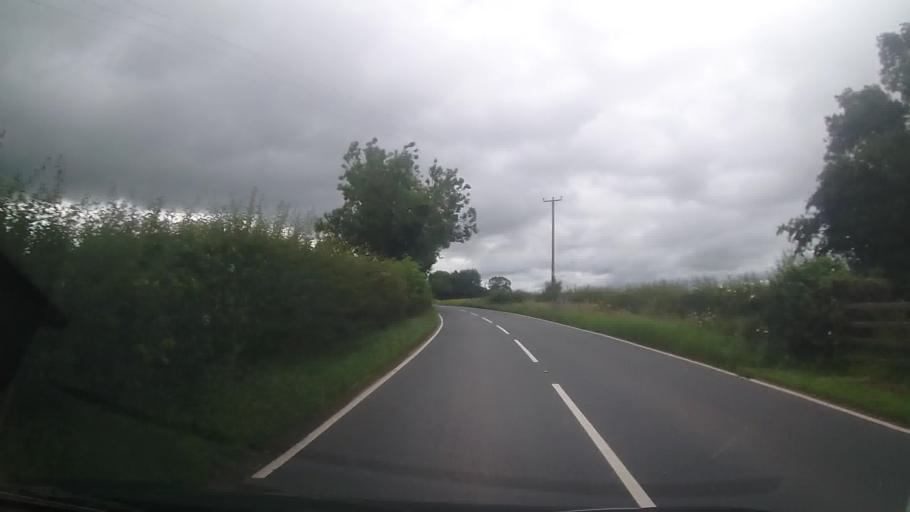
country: GB
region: England
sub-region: Shropshire
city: Whitchurch
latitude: 52.9604
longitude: -2.7347
